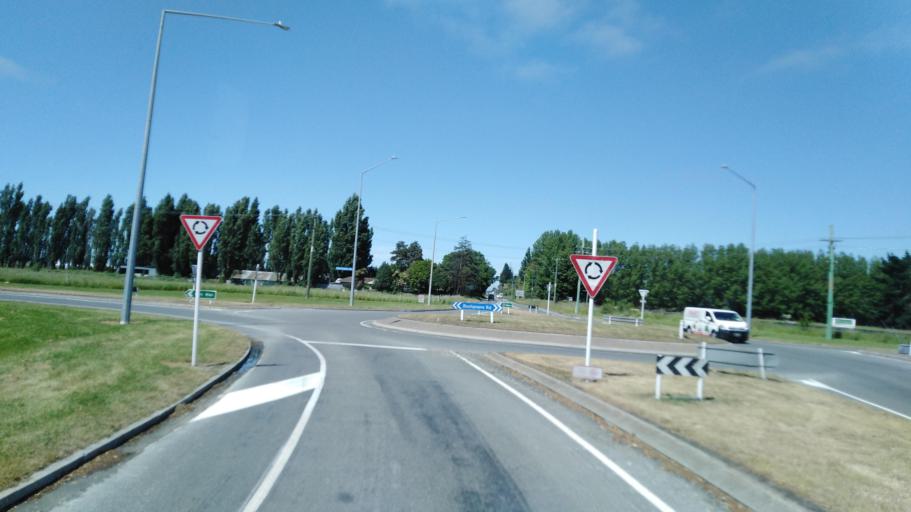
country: NZ
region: Canterbury
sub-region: Selwyn District
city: Prebbleton
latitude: -43.5192
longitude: 172.5051
